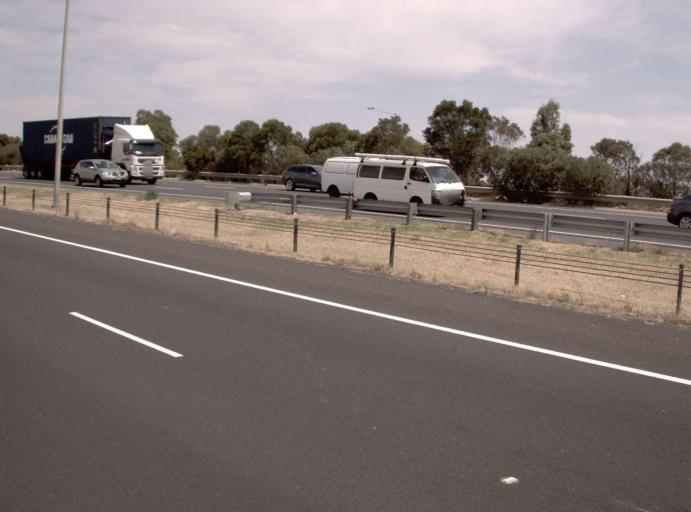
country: AU
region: Victoria
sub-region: Brimbank
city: Derrimut
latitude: -37.7968
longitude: 144.7883
